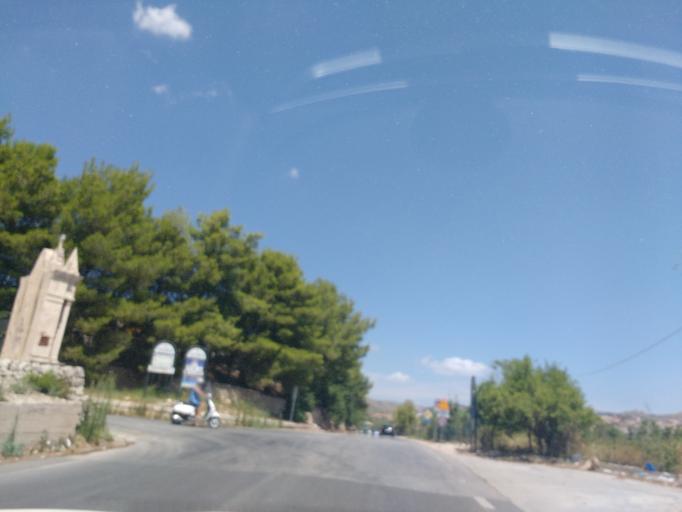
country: IT
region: Sicily
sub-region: Provincia di Siracusa
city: Noto
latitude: 36.8841
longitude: 15.0630
